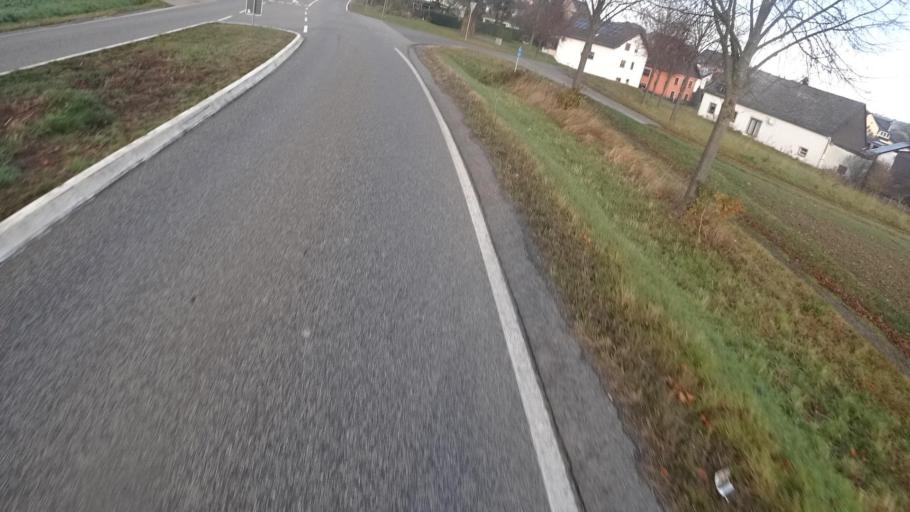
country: DE
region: Rheinland-Pfalz
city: Muhlpfad
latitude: 50.1195
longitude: 7.5565
